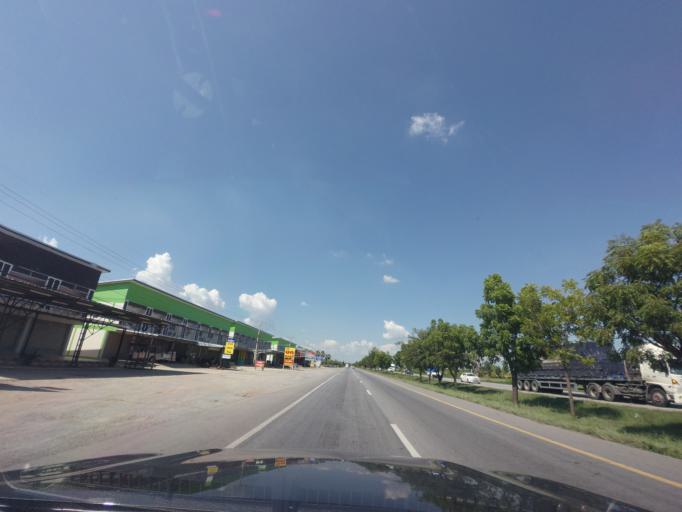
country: TH
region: Nakhon Ratchasima
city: Non Sung
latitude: 15.1747
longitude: 102.3363
